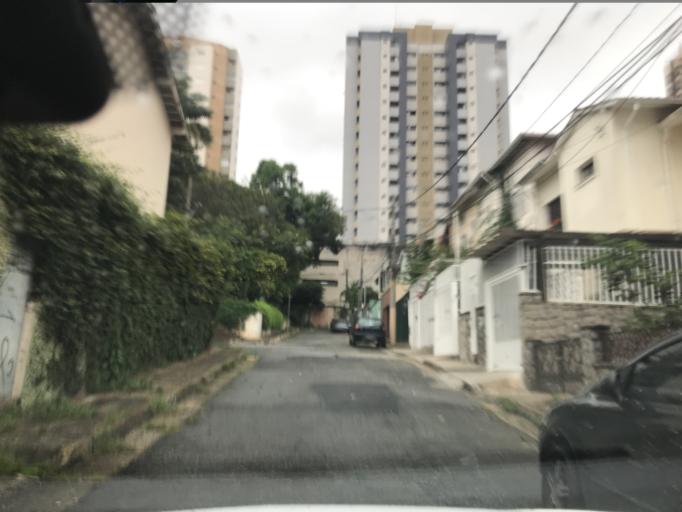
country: BR
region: Sao Paulo
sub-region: Sao Paulo
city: Sao Paulo
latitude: -23.5385
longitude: -46.6777
